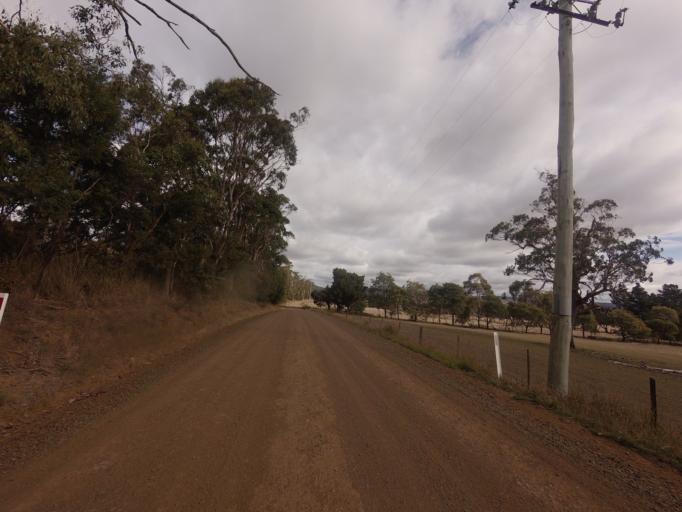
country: AU
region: Tasmania
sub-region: Brighton
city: Bridgewater
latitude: -42.4114
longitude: 147.3995
